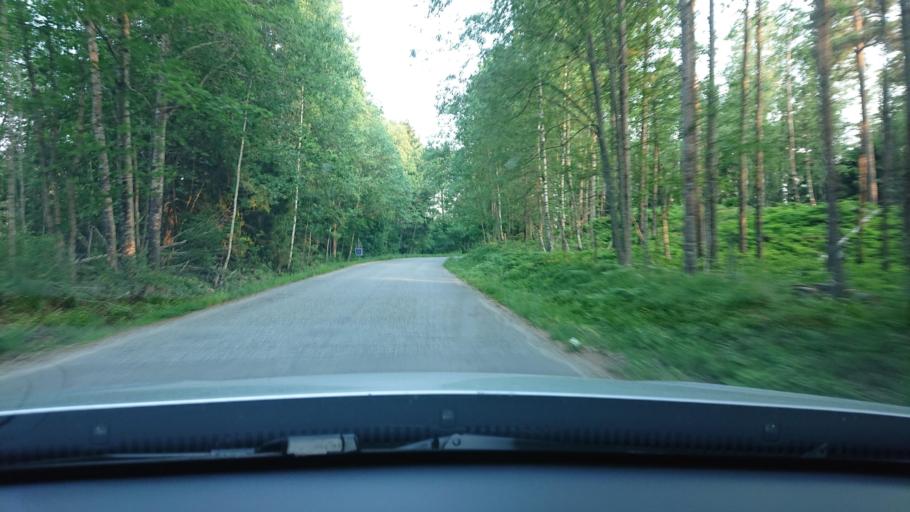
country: SE
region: Stockholm
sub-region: Osterakers Kommun
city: Akersberga
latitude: 59.5119
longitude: 18.3154
